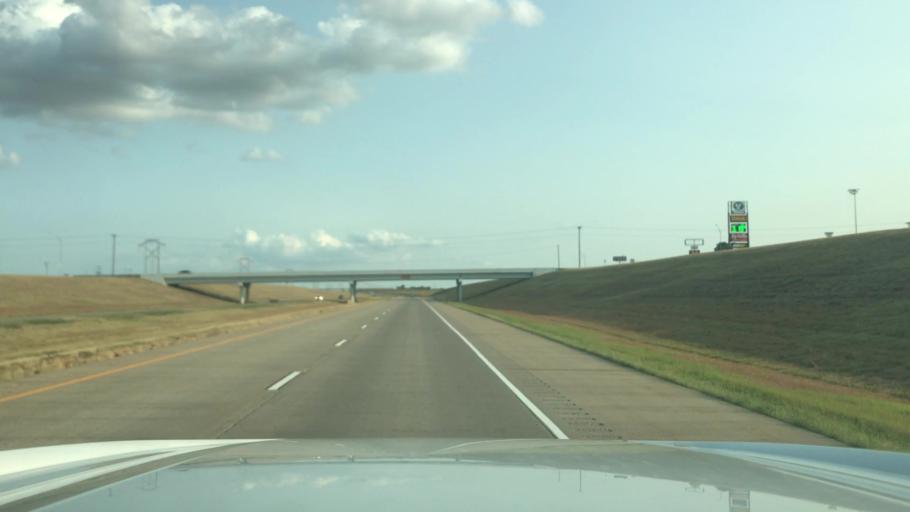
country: US
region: Texas
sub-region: Swisher County
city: Tulia
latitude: 34.5313
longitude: -101.7956
